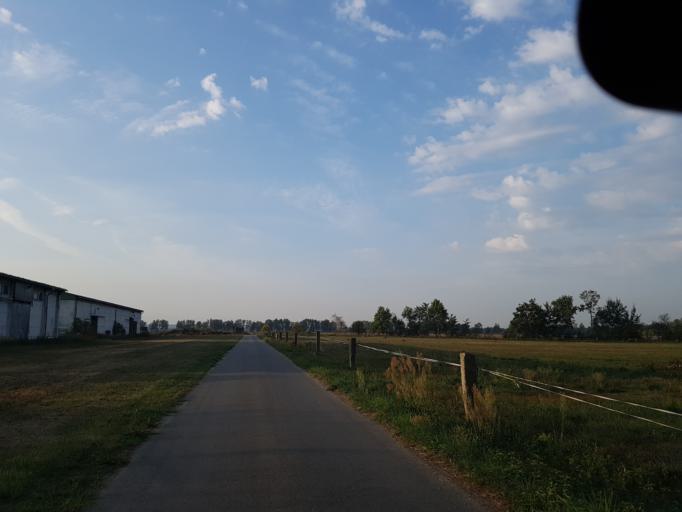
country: DE
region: Brandenburg
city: Hohenleipisch
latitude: 51.4614
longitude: 13.5664
